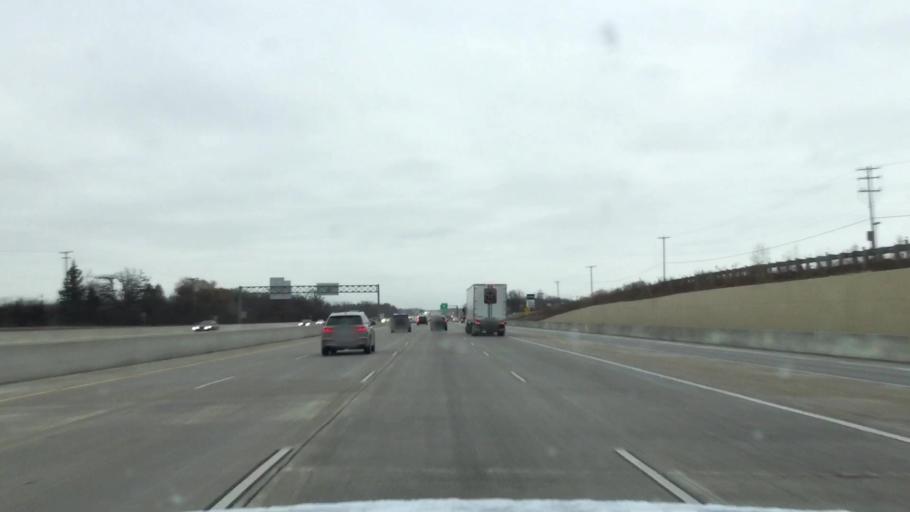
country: US
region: Wisconsin
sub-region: Kenosha County
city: Pleasant Prairie
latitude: 42.5637
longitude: -87.9528
